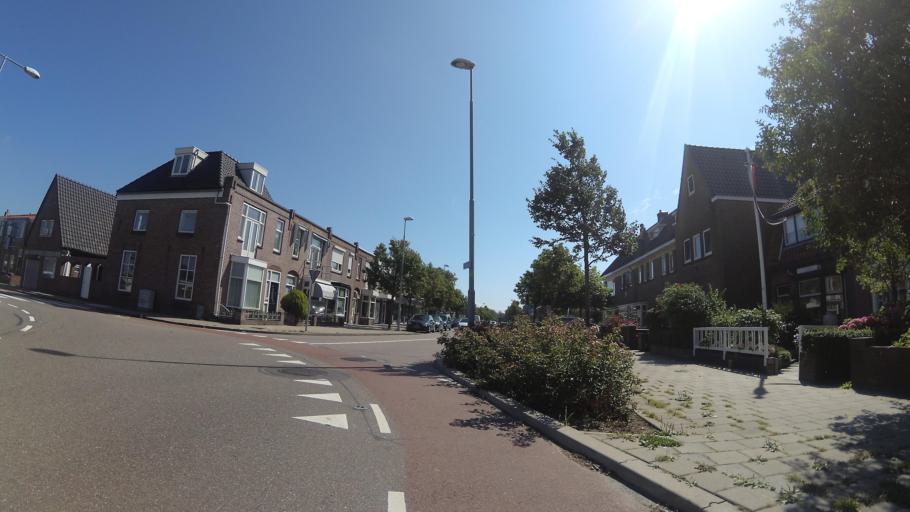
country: NL
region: North Holland
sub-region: Gemeente Den Helder
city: Den Helder
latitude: 52.9537
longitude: 4.7650
